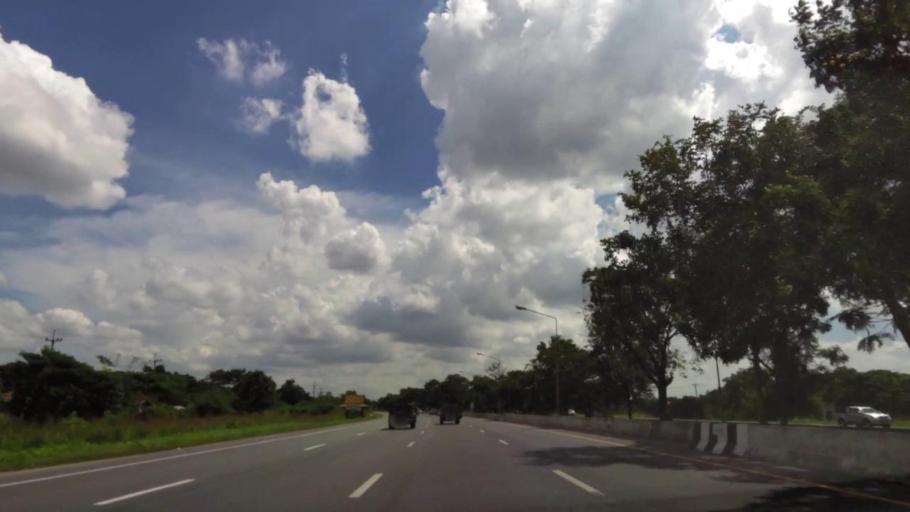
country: TH
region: Phra Nakhon Si Ayutthaya
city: Bang Pahan
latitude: 14.4406
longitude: 100.5427
